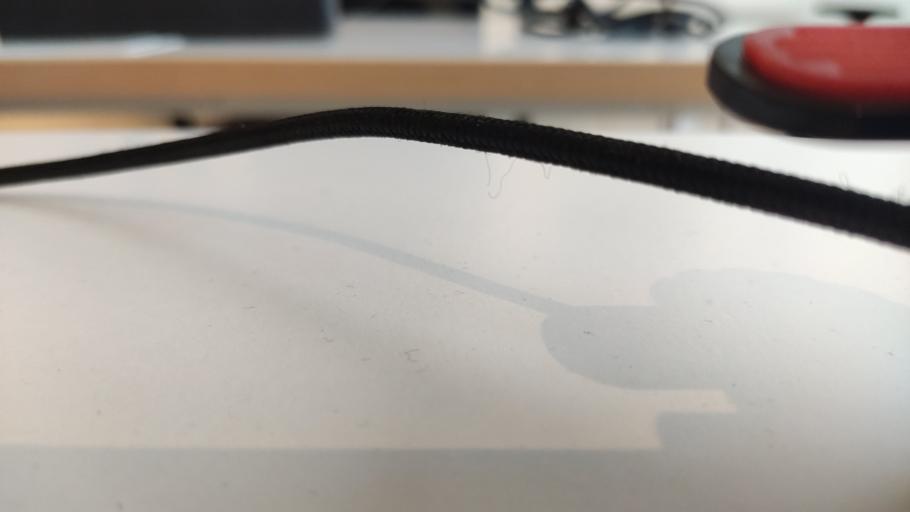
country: RU
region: Moskovskaya
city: Klin
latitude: 56.3418
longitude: 36.7450
